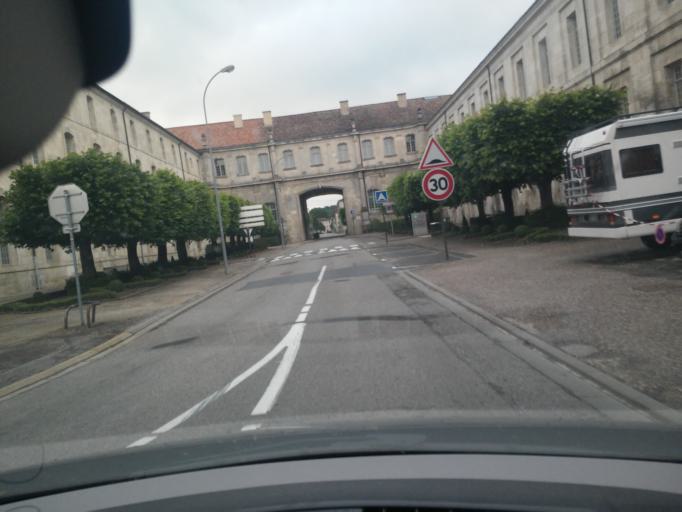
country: FR
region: Lorraine
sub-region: Departement de la Meuse
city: Saint-Mihiel
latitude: 48.8887
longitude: 5.5406
